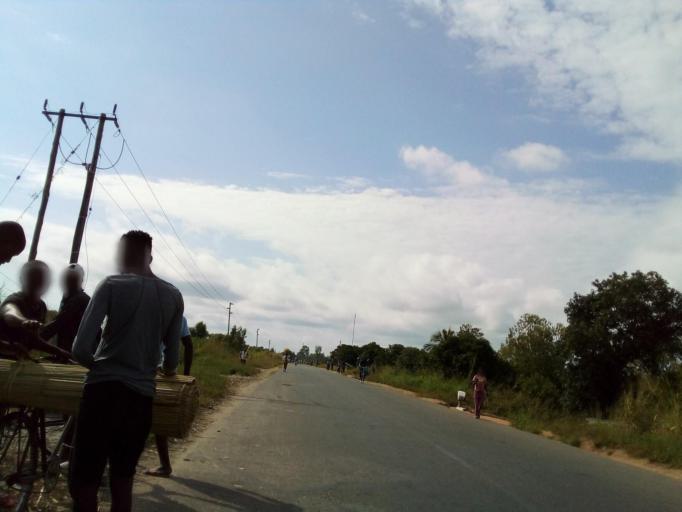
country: MZ
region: Zambezia
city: Quelimane
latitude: -17.5780
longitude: 36.6932
